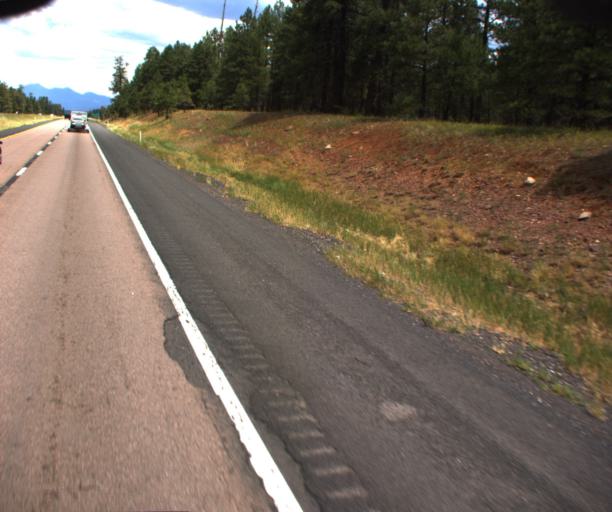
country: US
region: Arizona
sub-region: Coconino County
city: Mountainaire
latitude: 34.9963
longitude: -111.6866
